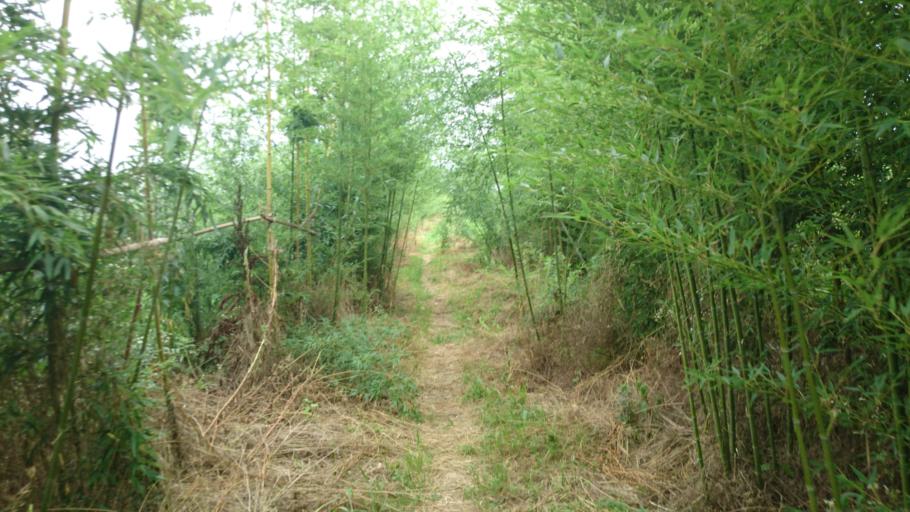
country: KR
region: Daegu
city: Hwawon
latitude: 35.8524
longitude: 128.4701
